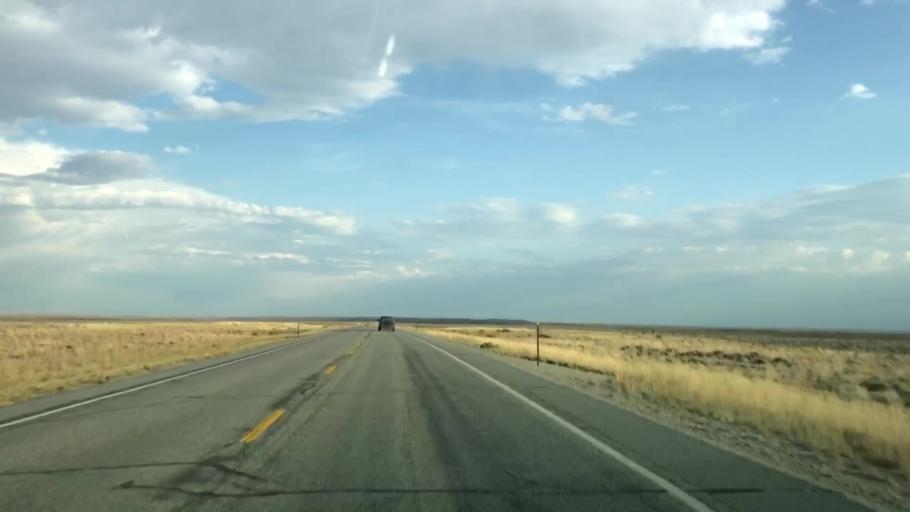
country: US
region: Wyoming
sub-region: Sublette County
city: Marbleton
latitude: 42.3360
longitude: -109.5197
